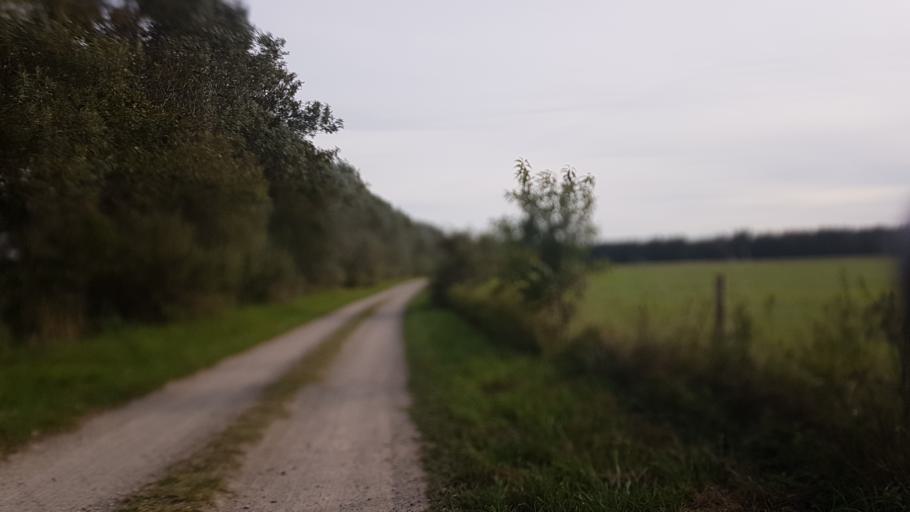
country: DE
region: Mecklenburg-Vorpommern
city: Gingst
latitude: 54.4824
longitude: 13.1611
